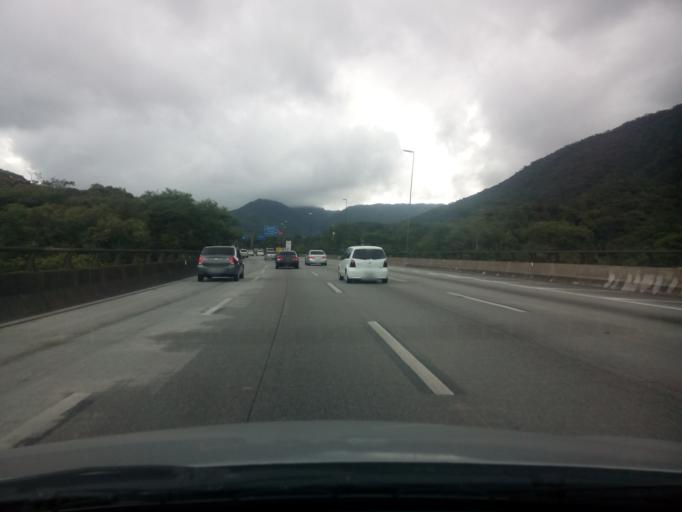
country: BR
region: Sao Paulo
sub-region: Cubatao
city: Cubatao
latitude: -23.8987
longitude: -46.4718
